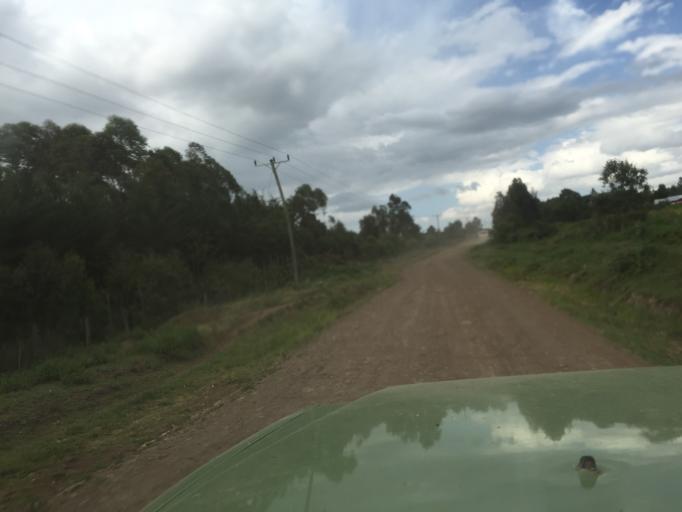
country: KE
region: Nyandarua
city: Ol Kalou
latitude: -0.4556
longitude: 36.4177
